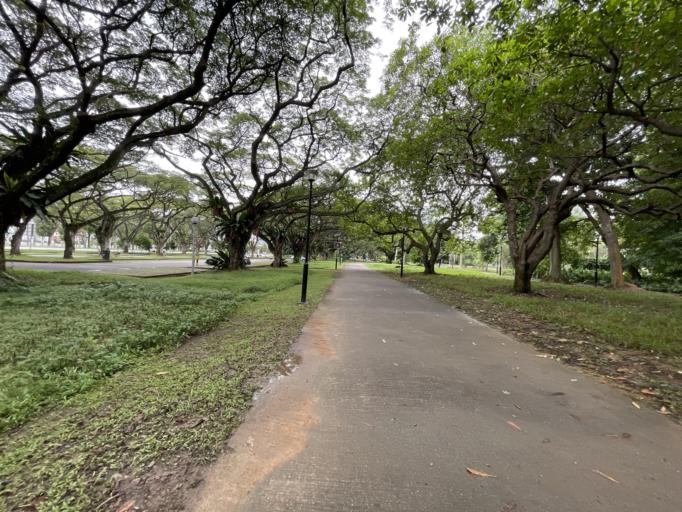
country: SG
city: Singapore
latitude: 1.2896
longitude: 103.7709
